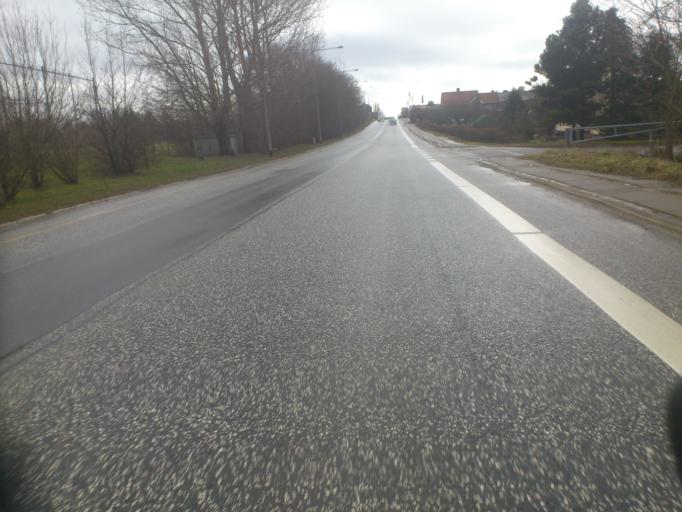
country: DK
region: South Denmark
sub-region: Fredericia Kommune
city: Fredericia
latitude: 55.5833
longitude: 9.7539
